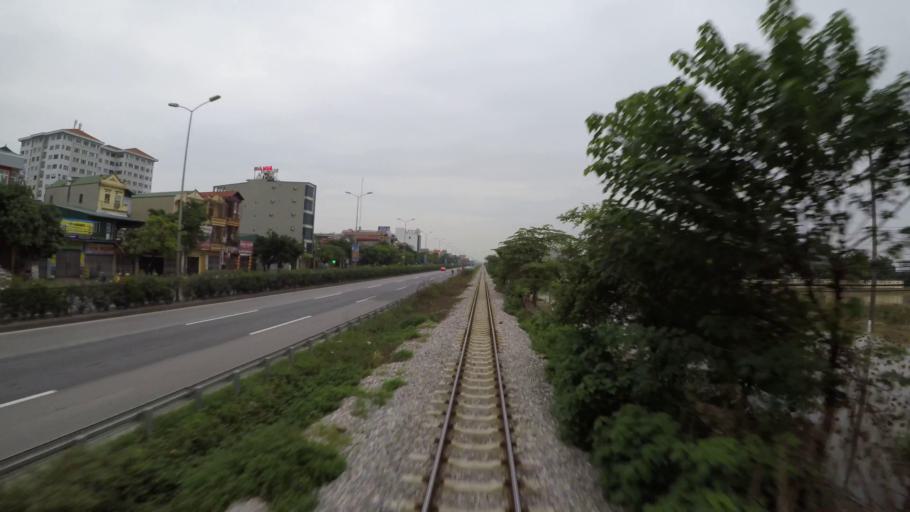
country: VN
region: Hung Yen
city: Nhu Quynh
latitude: 20.9837
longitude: 105.9791
